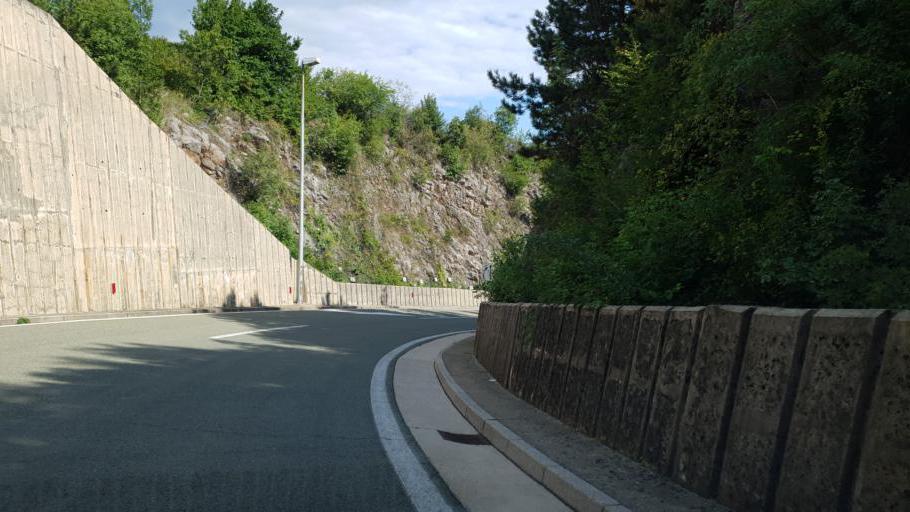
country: HR
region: Primorsko-Goranska
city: Matulji
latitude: 45.3636
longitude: 14.3335
